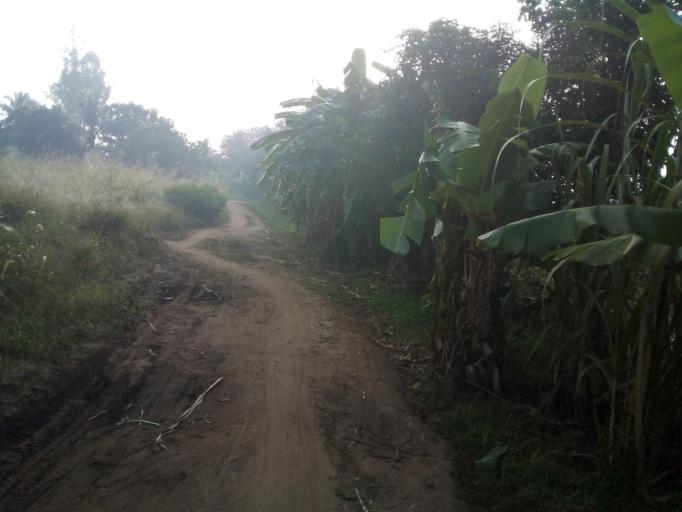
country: MZ
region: Zambezia
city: Quelimane
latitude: -17.5863
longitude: 36.6868
